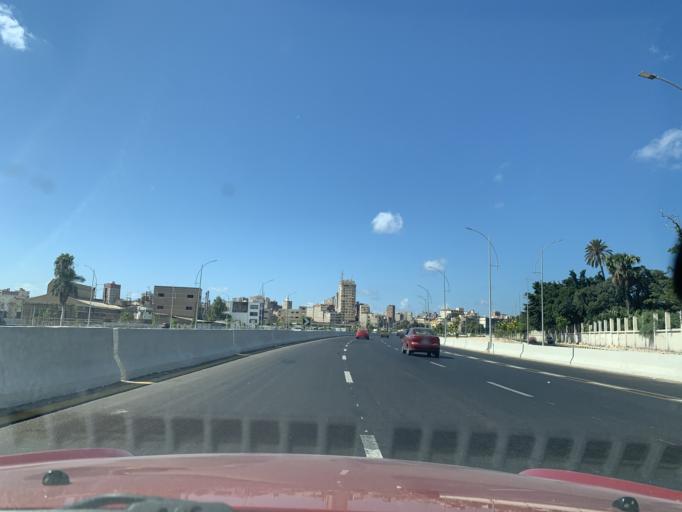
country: EG
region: Alexandria
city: Alexandria
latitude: 31.2004
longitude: 29.9474
